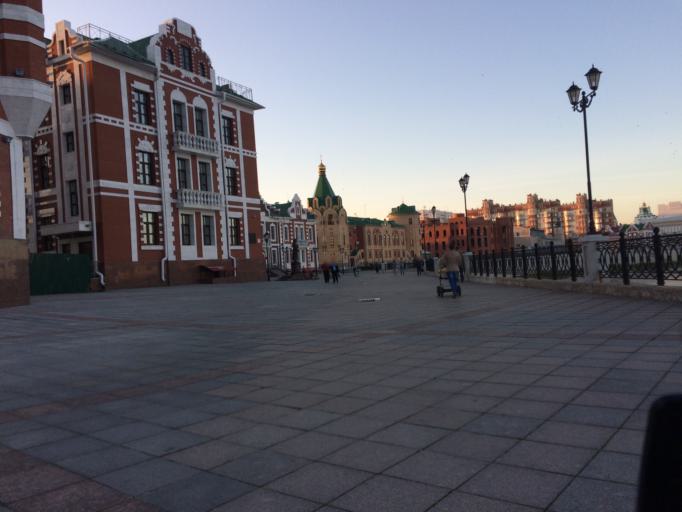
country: RU
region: Mariy-El
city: Yoshkar-Ola
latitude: 56.6306
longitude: 47.8993
